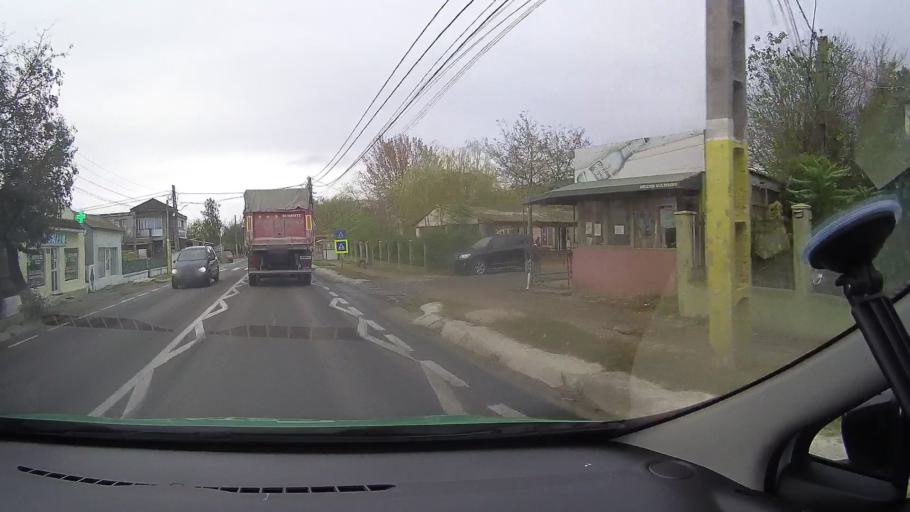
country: RO
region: Constanta
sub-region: Comuna Poarta Alba
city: Poarta Alba
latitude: 44.2065
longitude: 28.3948
